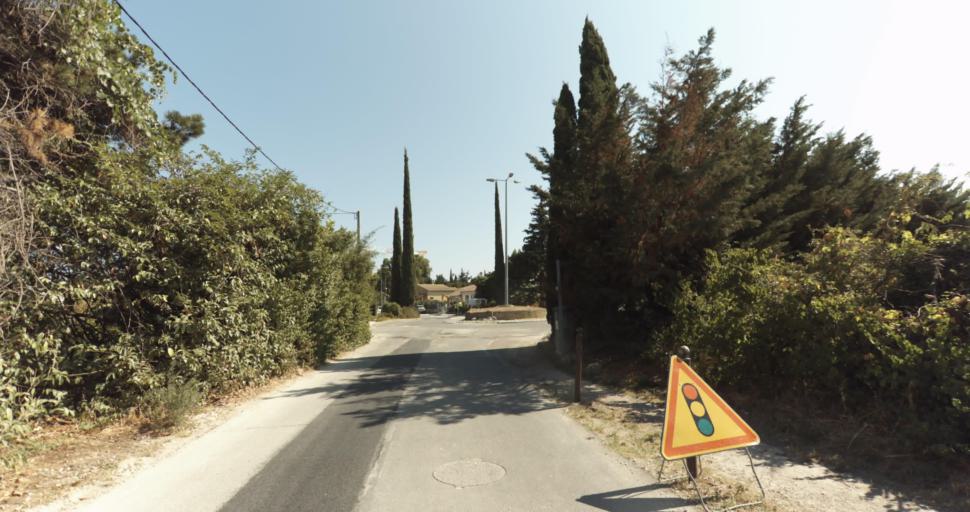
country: FR
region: Provence-Alpes-Cote d'Azur
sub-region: Departement du Vaucluse
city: Monteux
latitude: 44.0285
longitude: 4.9960
